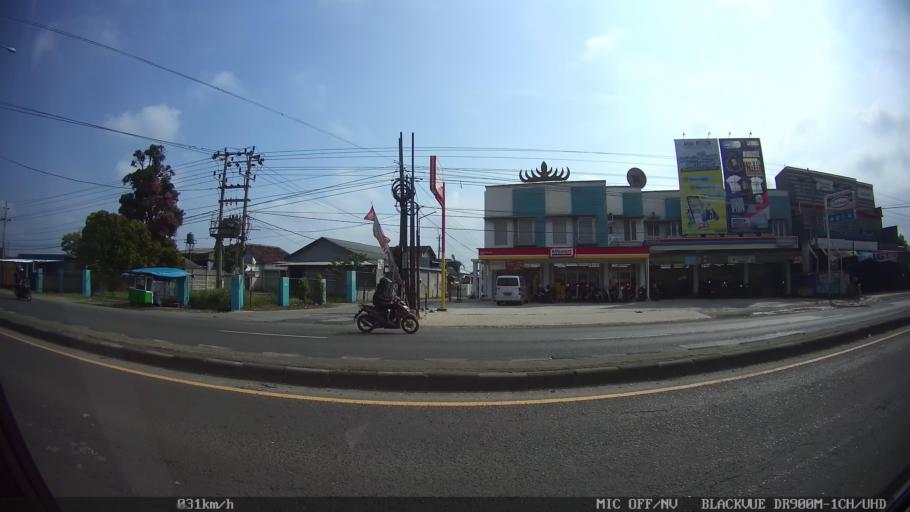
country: ID
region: Lampung
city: Kedaton
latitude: -5.3681
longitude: 105.2697
